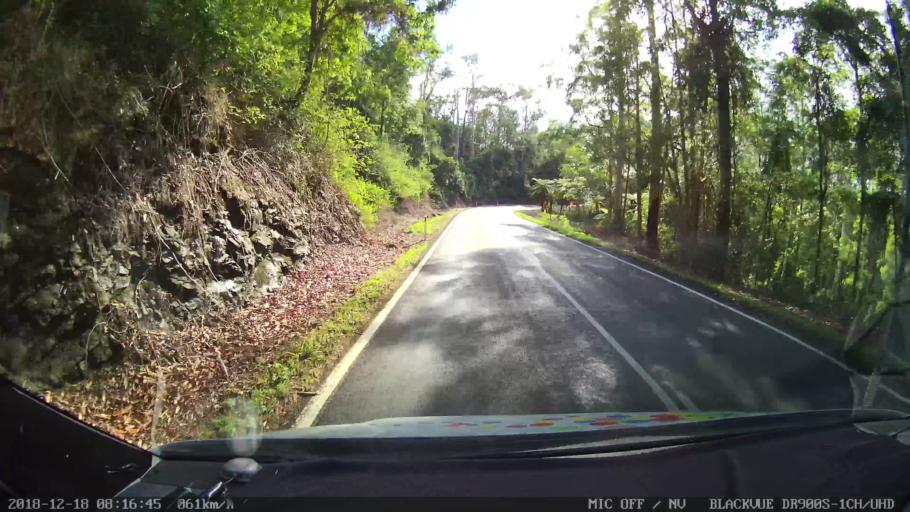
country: AU
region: New South Wales
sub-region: Kyogle
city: Kyogle
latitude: -28.3365
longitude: 152.6962
